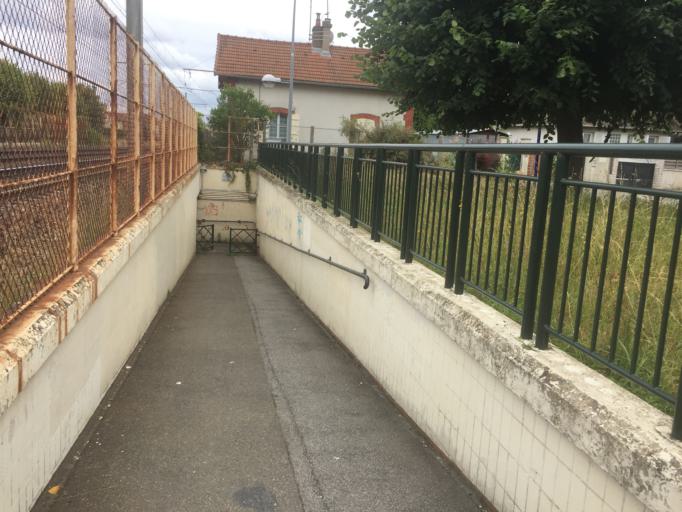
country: FR
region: Ile-de-France
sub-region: Departement des Yvelines
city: Les Clayes-sous-Bois
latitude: 48.8299
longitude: 1.9830
